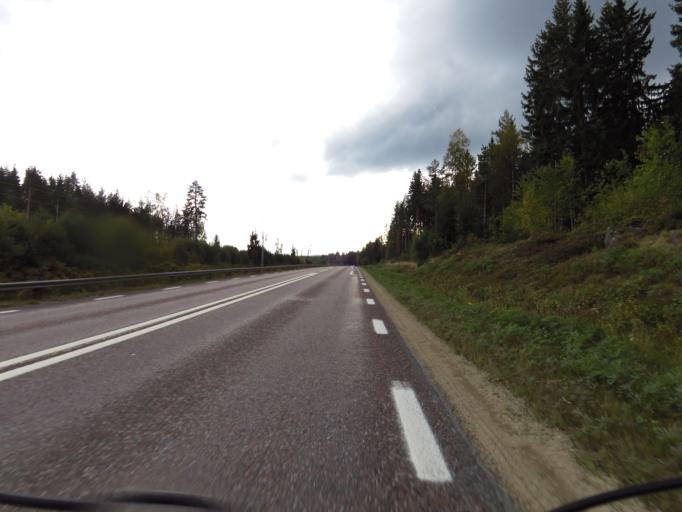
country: SE
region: Gaevleborg
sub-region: Ockelbo Kommun
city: Ockelbo
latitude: 60.8703
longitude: 16.7019
